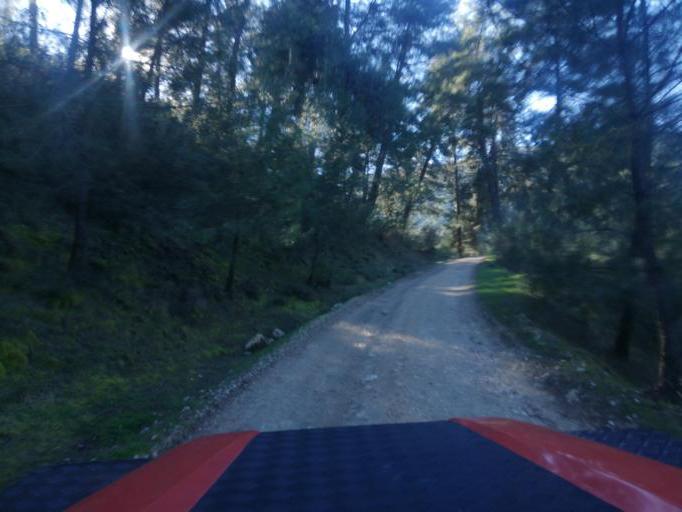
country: TR
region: Antalya
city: Kas
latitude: 36.2975
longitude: 29.6879
